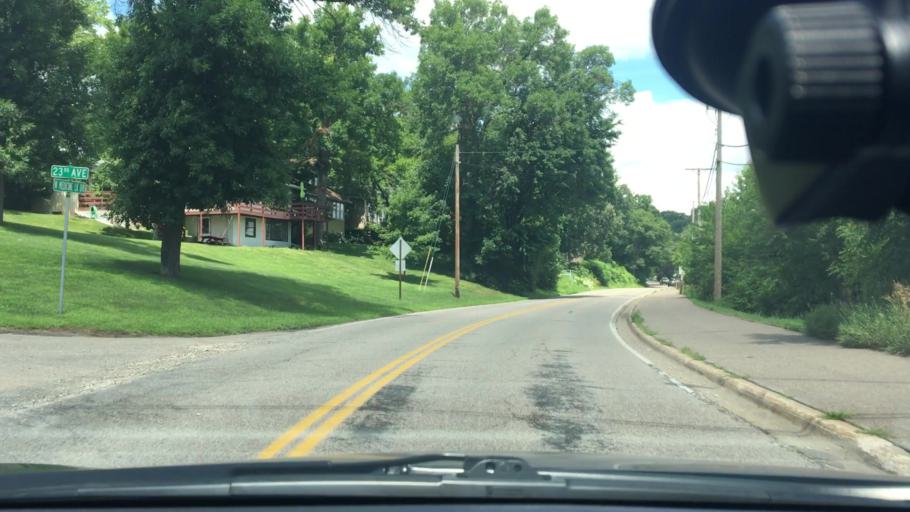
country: US
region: Minnesota
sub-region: Hennepin County
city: Plymouth
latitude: 45.0036
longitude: -93.4306
